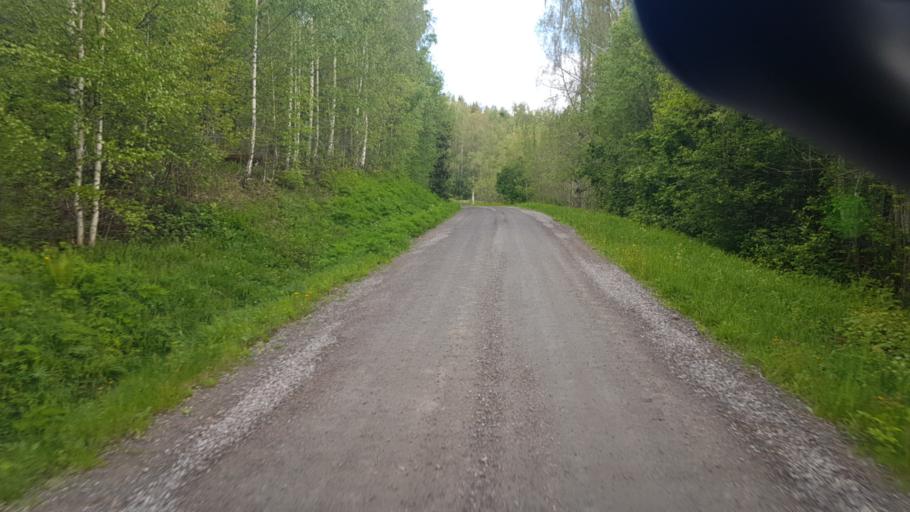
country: NO
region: Hedmark
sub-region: Eidskog
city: Skotterud
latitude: 59.8712
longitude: 11.9726
